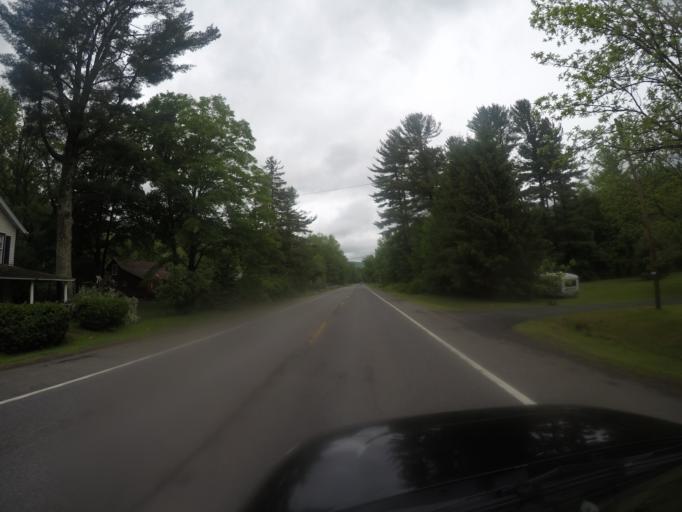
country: US
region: New York
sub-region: Ulster County
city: Shokan
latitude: 42.0985
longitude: -74.3420
